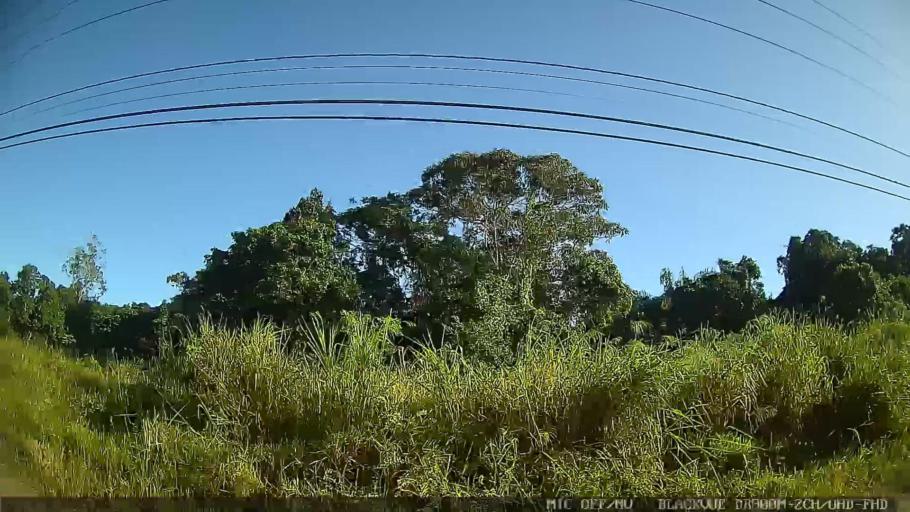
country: BR
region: Sao Paulo
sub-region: Itanhaem
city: Itanhaem
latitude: -24.2126
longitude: -46.8665
